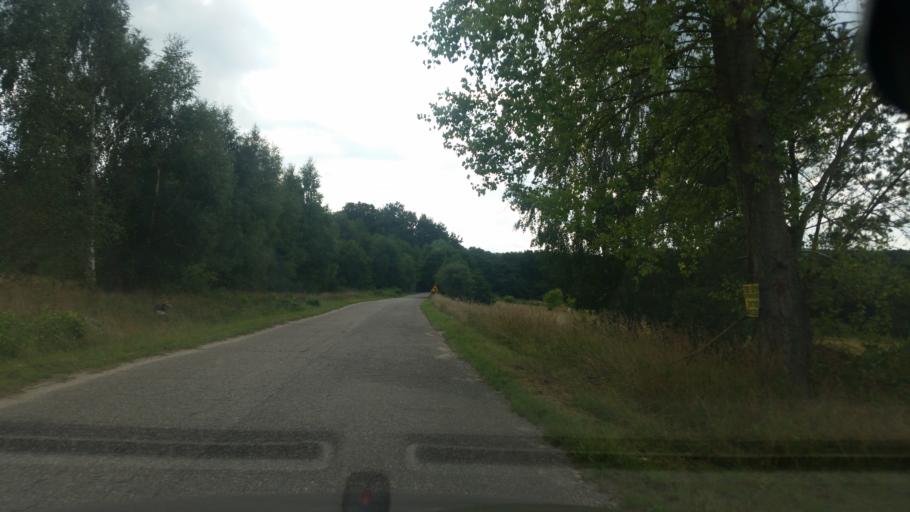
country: PL
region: Pomeranian Voivodeship
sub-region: Powiat wejherowski
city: Choczewo
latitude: 54.7627
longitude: 17.7925
